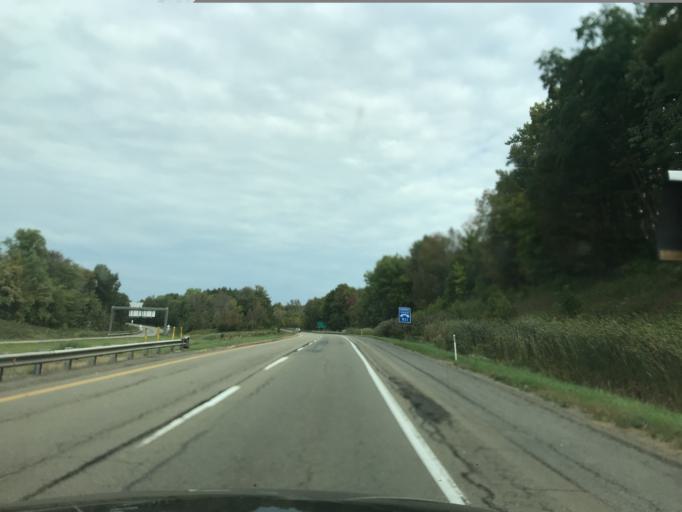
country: US
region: Pennsylvania
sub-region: Erie County
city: Erie
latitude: 42.0457
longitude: -80.1155
